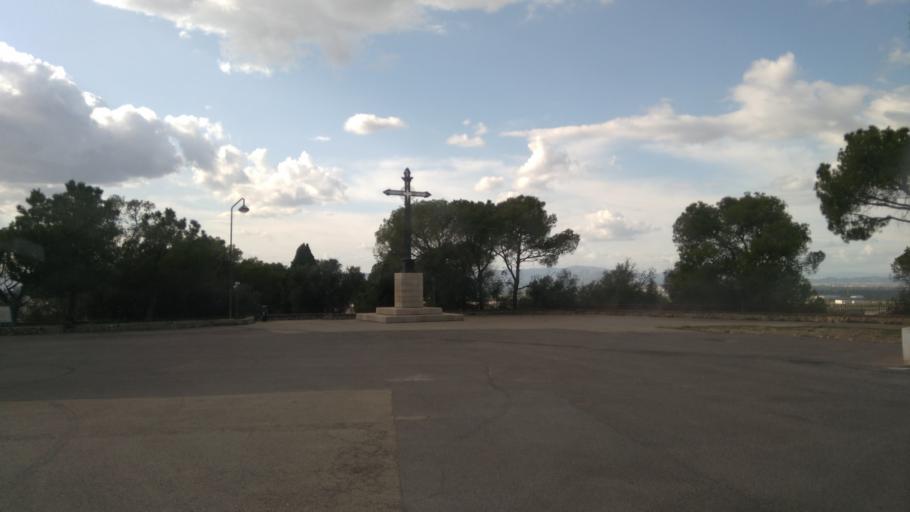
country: ES
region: Valencia
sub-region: Provincia de Valencia
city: Alzira
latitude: 39.1528
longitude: -0.4194
